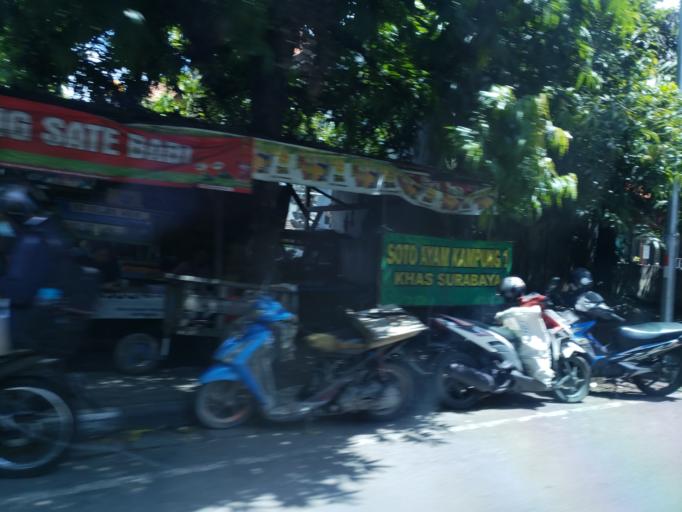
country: ID
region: Bali
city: Kelanabian
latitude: -8.7604
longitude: 115.1760
